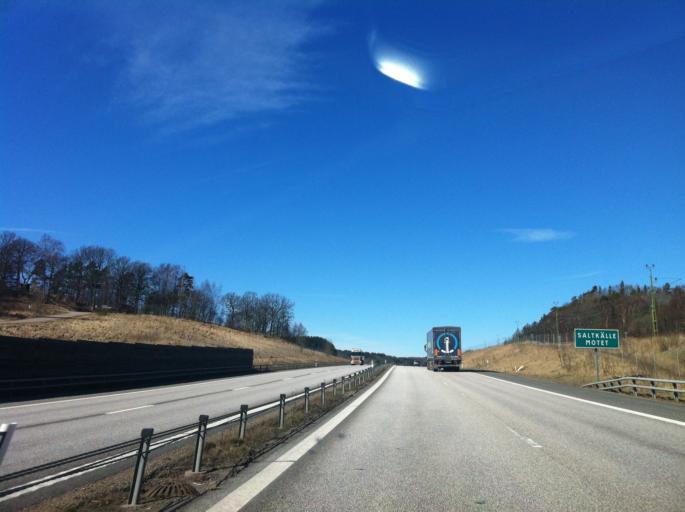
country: SE
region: Vaestra Goetaland
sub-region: Munkedals Kommun
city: Munkedal
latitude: 58.3807
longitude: 11.7739
